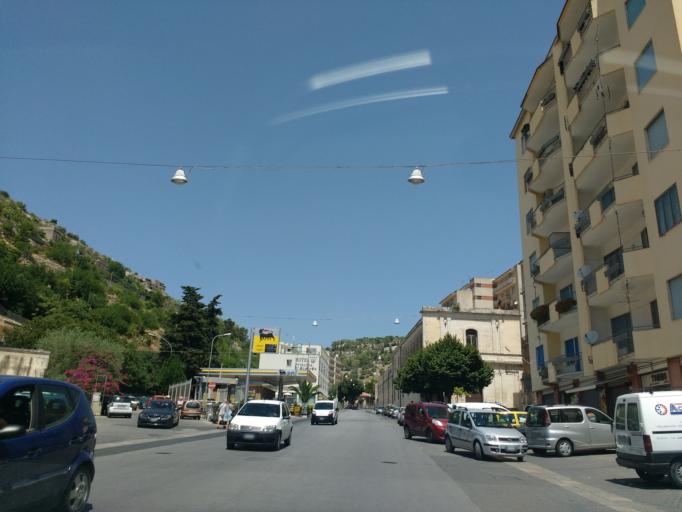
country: IT
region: Sicily
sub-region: Ragusa
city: Modica
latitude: 36.8644
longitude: 14.7590
